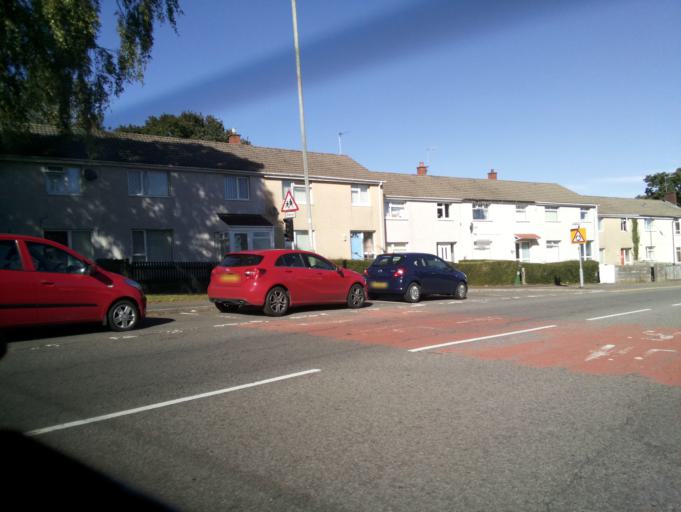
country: GB
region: Wales
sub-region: Torfaen County Borough
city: Cwmbran
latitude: 51.6447
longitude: -3.0392
